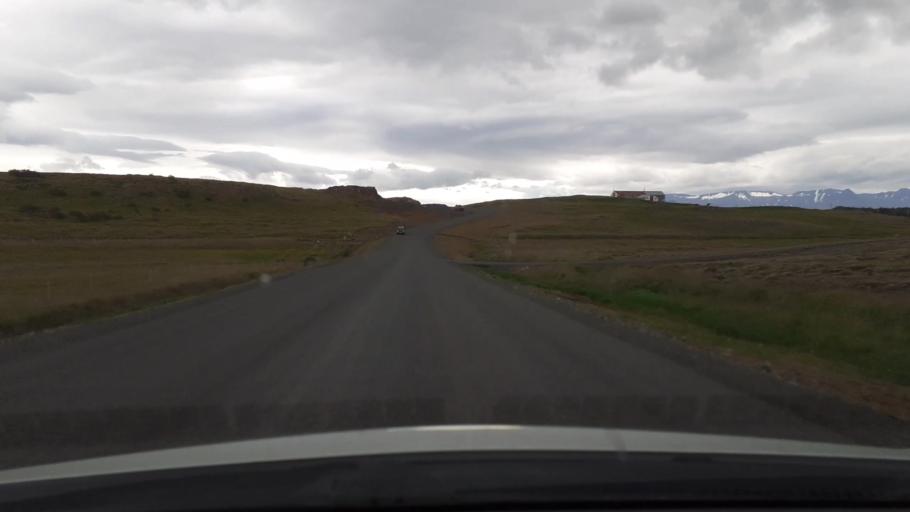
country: IS
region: West
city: Borgarnes
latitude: 64.6717
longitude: -21.7024
